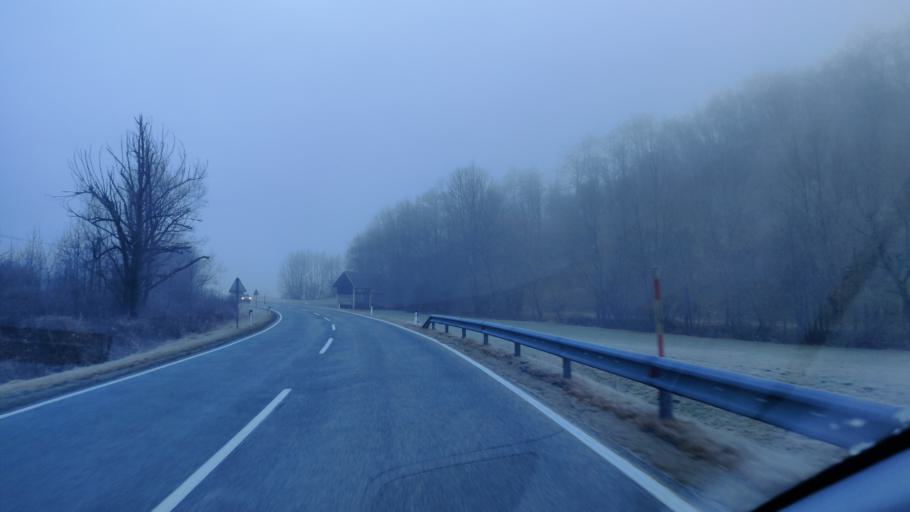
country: SI
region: Bohinj
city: Bohinjska Bistrica
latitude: 46.2874
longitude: 14.0153
